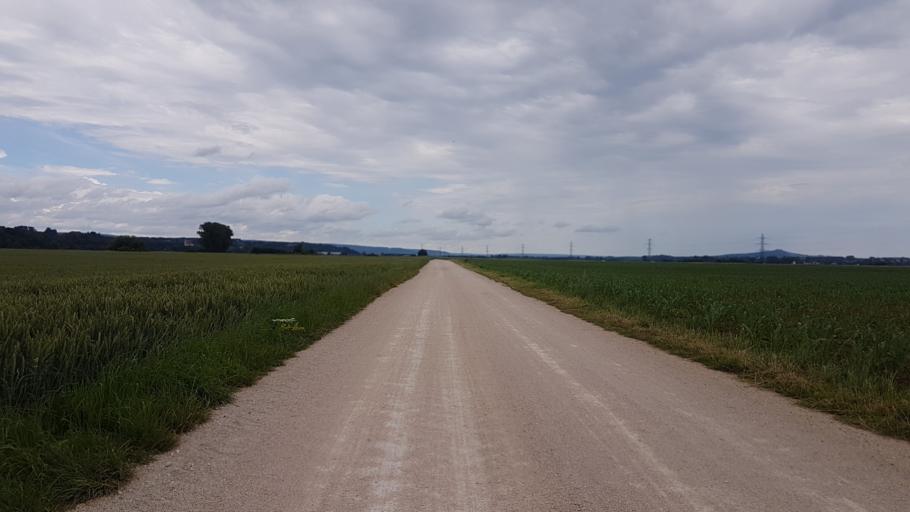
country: DE
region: Baden-Wuerttemberg
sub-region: Tuebingen Region
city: Herbertingen
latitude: 48.0804
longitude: 9.4174
